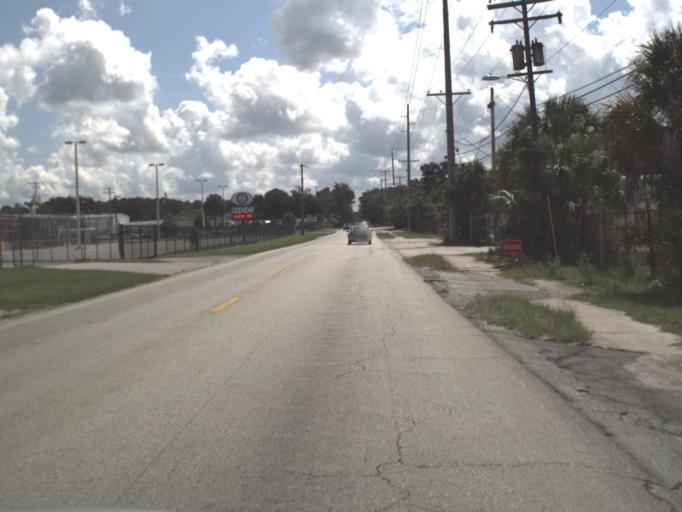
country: US
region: Florida
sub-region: Hillsborough County
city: East Lake-Orient Park
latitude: 27.9668
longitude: -82.3934
